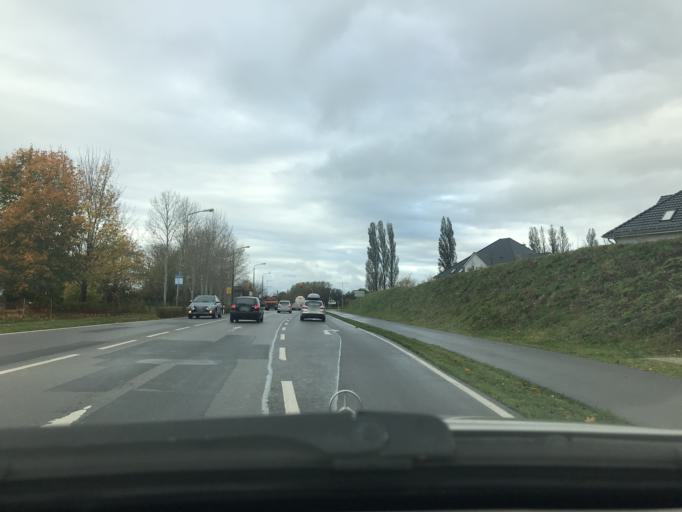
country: DE
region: Mecklenburg-Vorpommern
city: Ostseebad Zinnowitz
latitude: 54.0684
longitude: 13.9127
